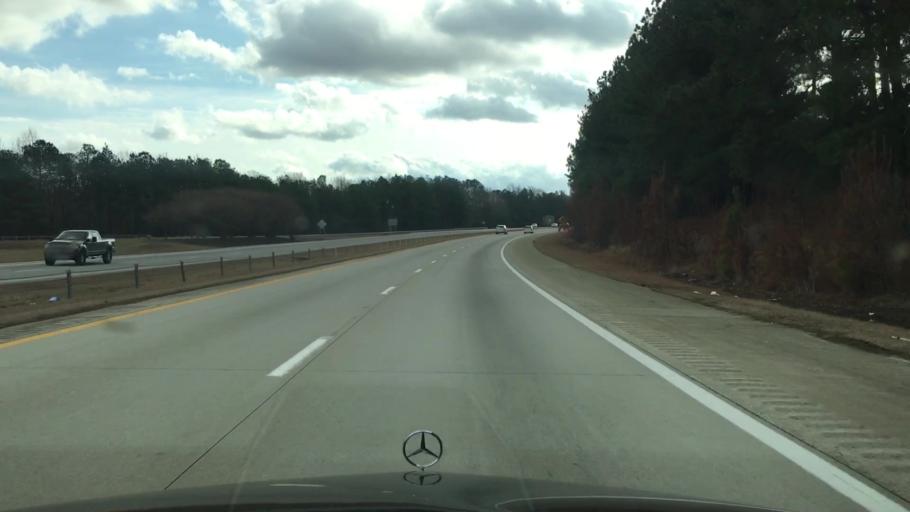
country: US
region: North Carolina
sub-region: Johnston County
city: Clayton
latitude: 35.6060
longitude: -78.5639
